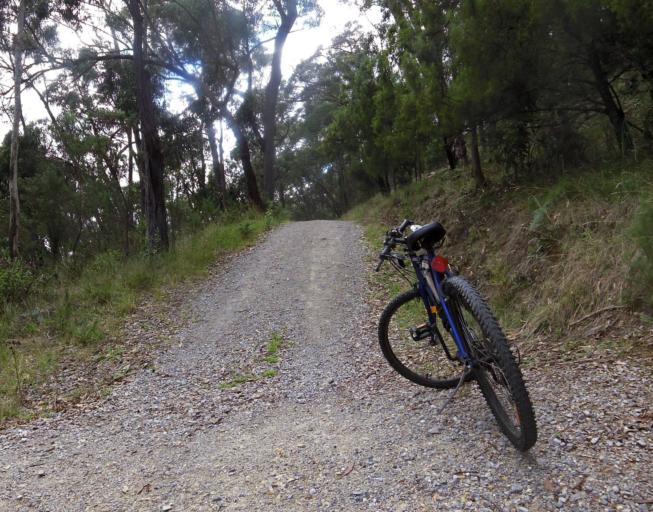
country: AU
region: Victoria
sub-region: Yarra Ranges
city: Montrose
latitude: -37.8263
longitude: 145.3459
